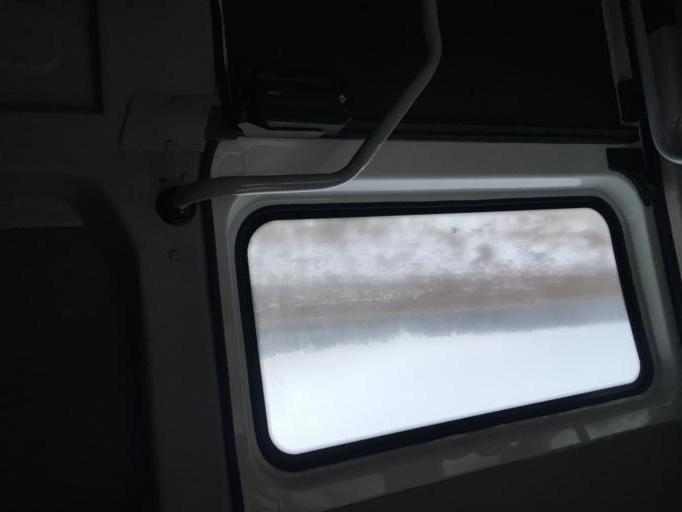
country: RU
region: Tula
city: Krapivna
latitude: 54.1188
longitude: 37.2260
